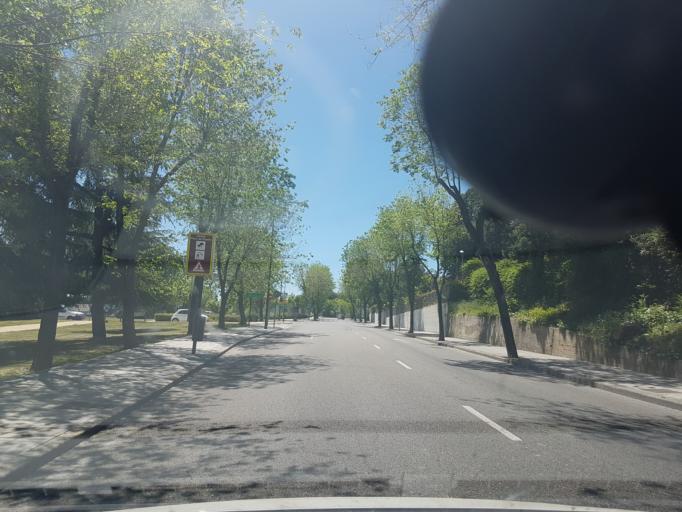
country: ES
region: Madrid
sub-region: Provincia de Madrid
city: Pozuelo de Alarcon
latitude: 40.4410
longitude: -3.8078
